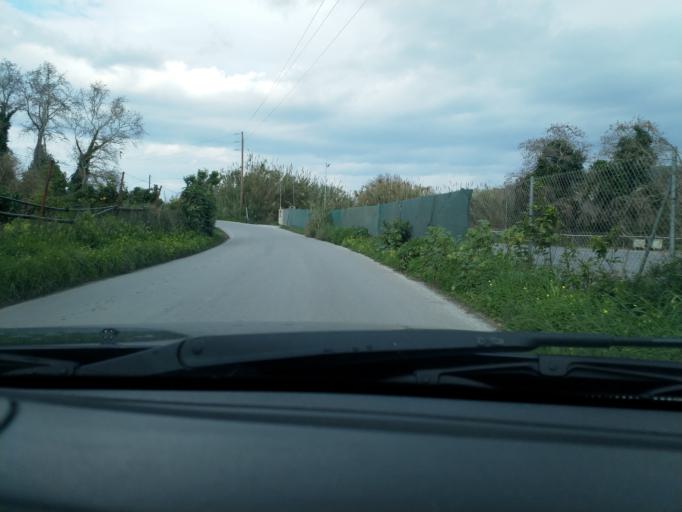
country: GR
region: Crete
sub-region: Nomos Chanias
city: Gerani
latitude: 35.5044
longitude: 23.8961
